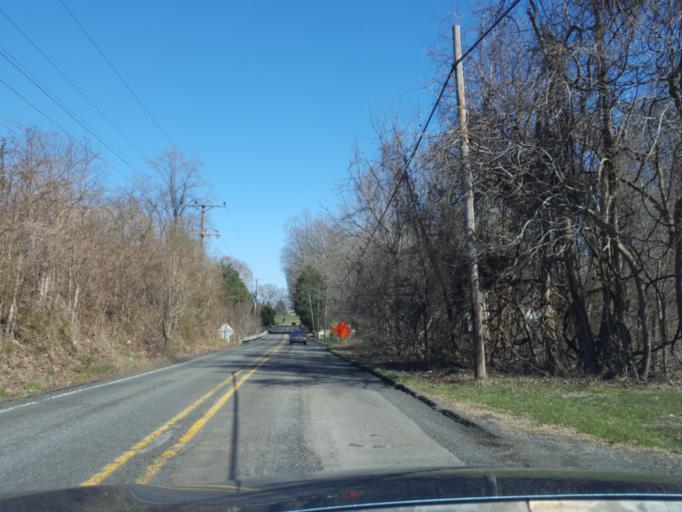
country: US
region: Maryland
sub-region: Anne Arundel County
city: Deale
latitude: 38.7802
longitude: -76.5823
